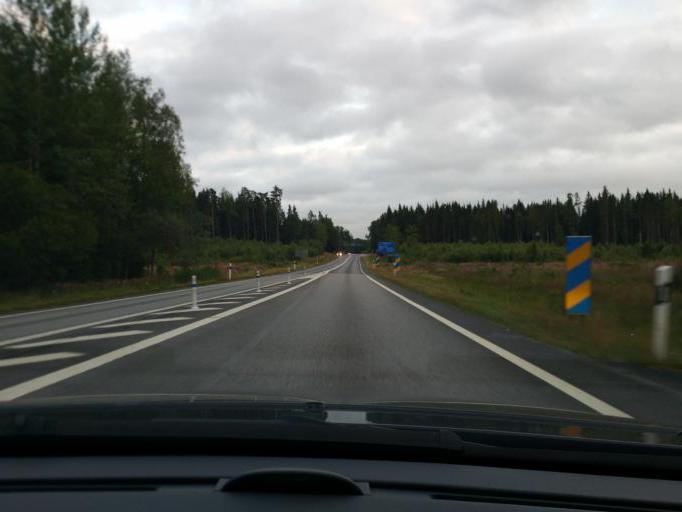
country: SE
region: Kronoberg
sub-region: Vaxjo Kommun
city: Lammhult
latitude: 57.0948
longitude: 14.6393
